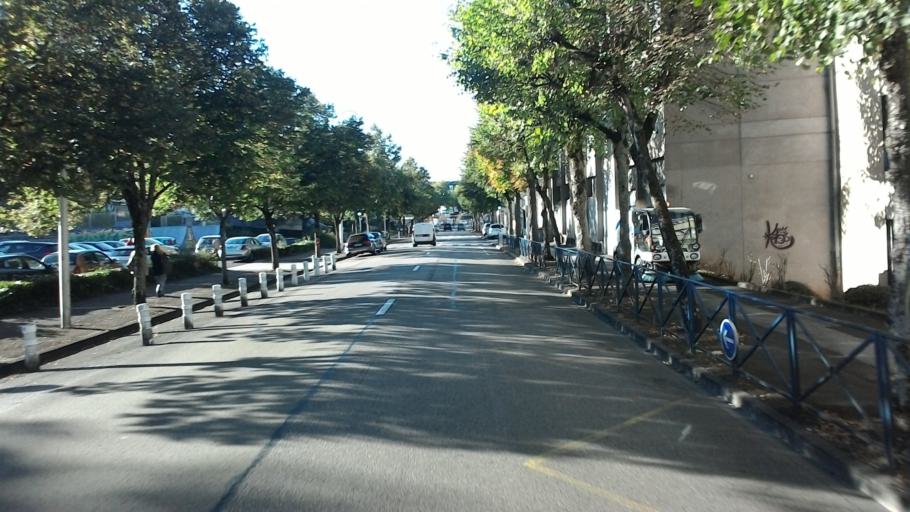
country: FR
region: Champagne-Ardenne
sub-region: Departement de la Haute-Marne
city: Chaumont
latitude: 48.1119
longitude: 5.1427
